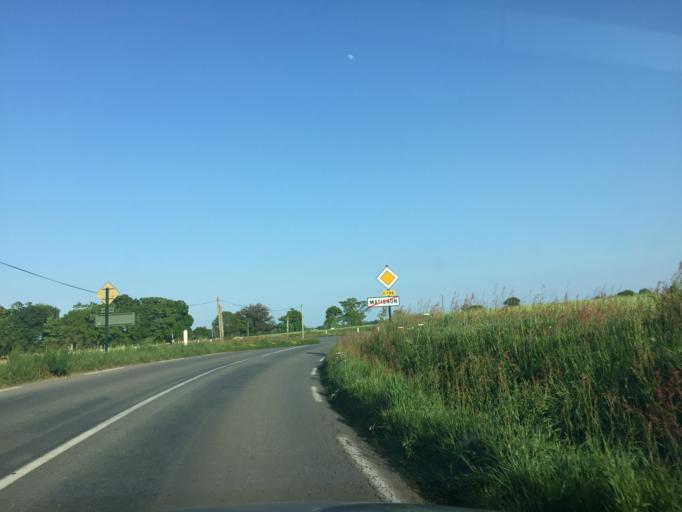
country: FR
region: Brittany
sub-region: Departement des Cotes-d'Armor
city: Matignon
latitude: 48.5978
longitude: -2.2847
